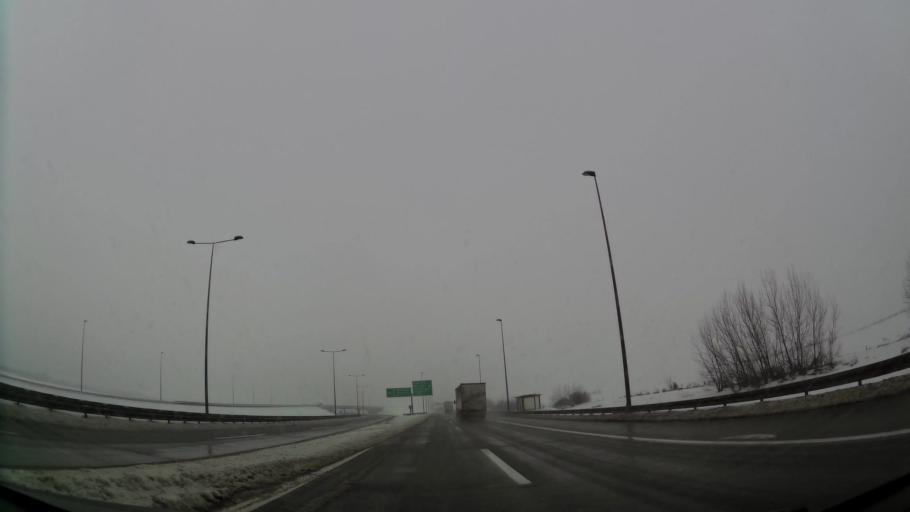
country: RS
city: Dobanovci
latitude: 44.8259
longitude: 20.2519
